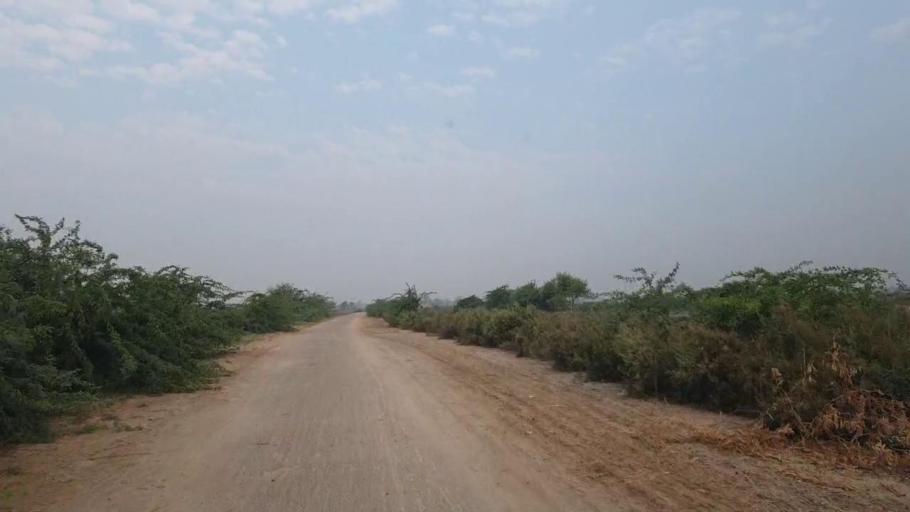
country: PK
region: Sindh
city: Tando Bago
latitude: 24.7796
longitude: 68.8907
